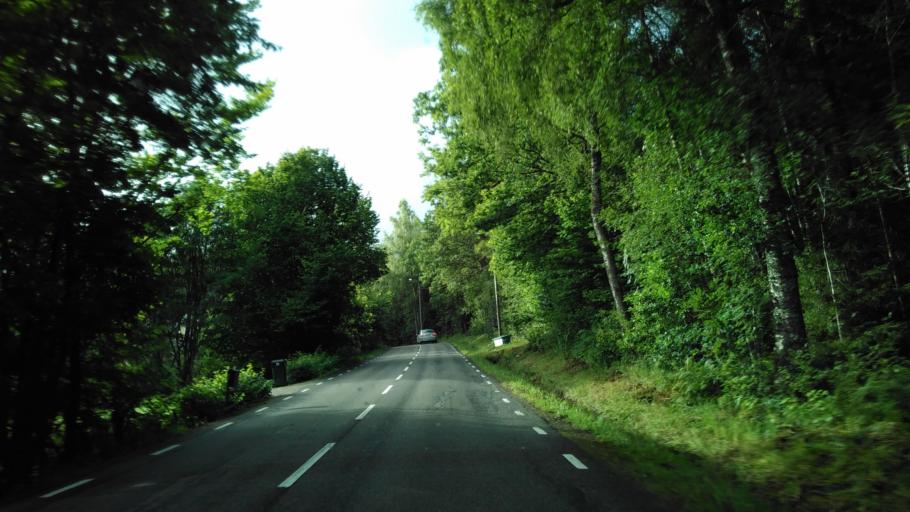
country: SE
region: Vaestra Goetaland
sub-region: Boras Kommun
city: Ganghester
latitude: 57.7928
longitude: 13.0141
